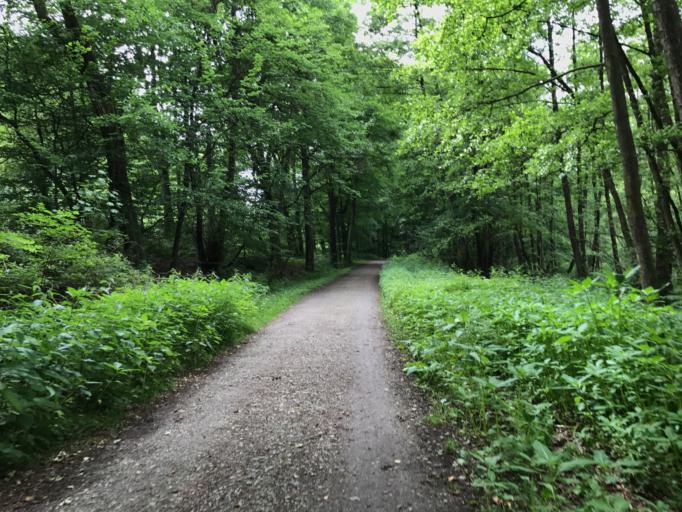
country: DE
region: North Rhine-Westphalia
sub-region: Regierungsbezirk Dusseldorf
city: Duisburg
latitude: 51.4165
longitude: 6.8112
